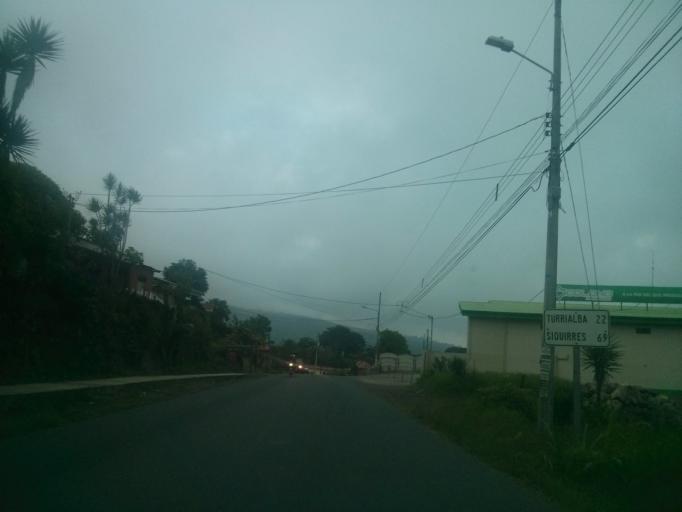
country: CR
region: Cartago
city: Cot
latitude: 9.8867
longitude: -83.8061
